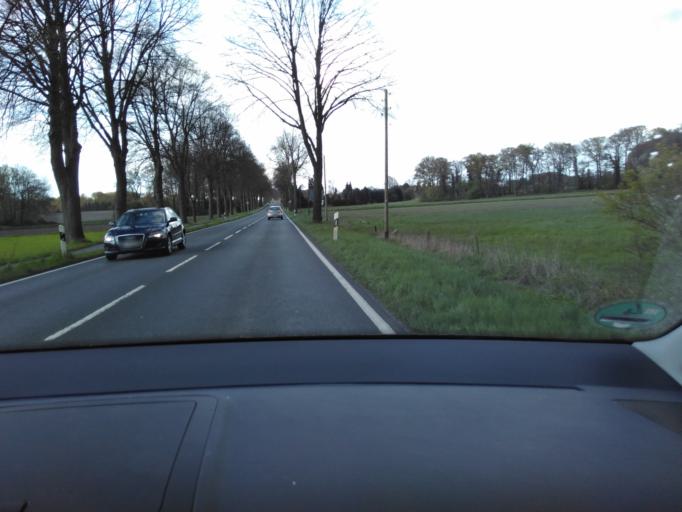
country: DE
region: North Rhine-Westphalia
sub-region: Regierungsbezirk Detmold
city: Steinhagen
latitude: 51.9540
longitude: 8.4419
